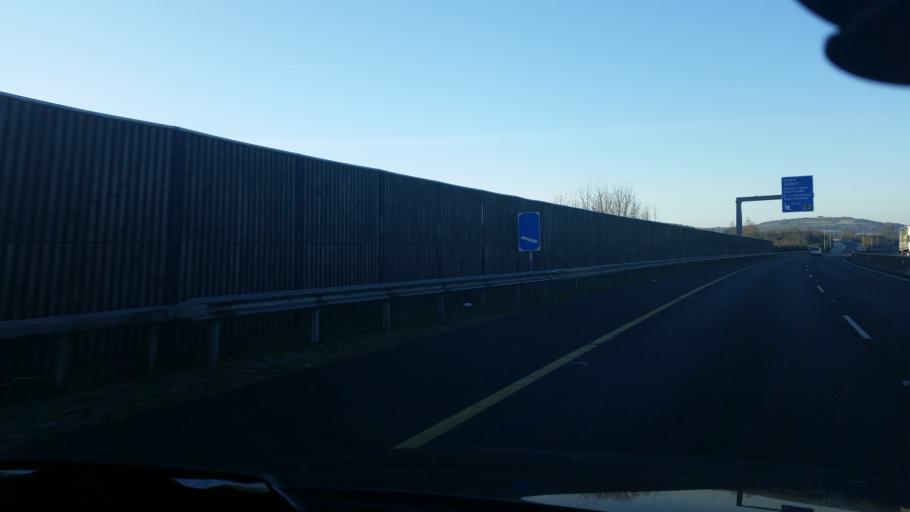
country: IE
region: Leinster
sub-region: Loch Garman
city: Gorey
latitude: 52.6663
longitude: -6.2652
